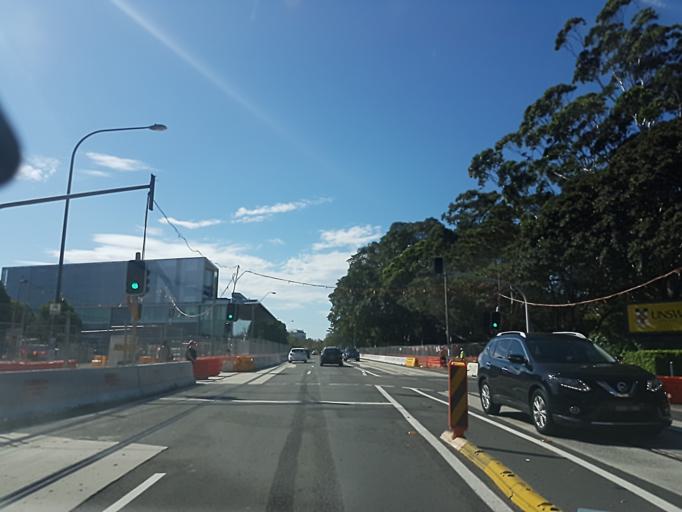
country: AU
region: New South Wales
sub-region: Randwick
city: Kensington
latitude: -33.9175
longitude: 151.2260
